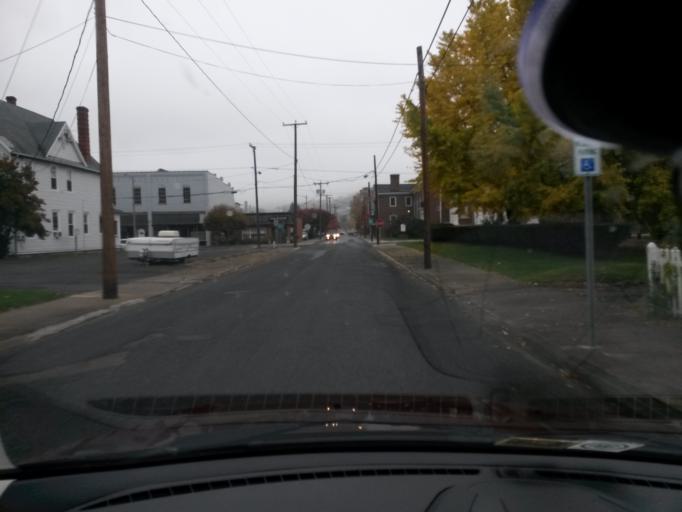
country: US
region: Virginia
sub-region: City of Covington
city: Covington
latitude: 37.7903
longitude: -79.9967
